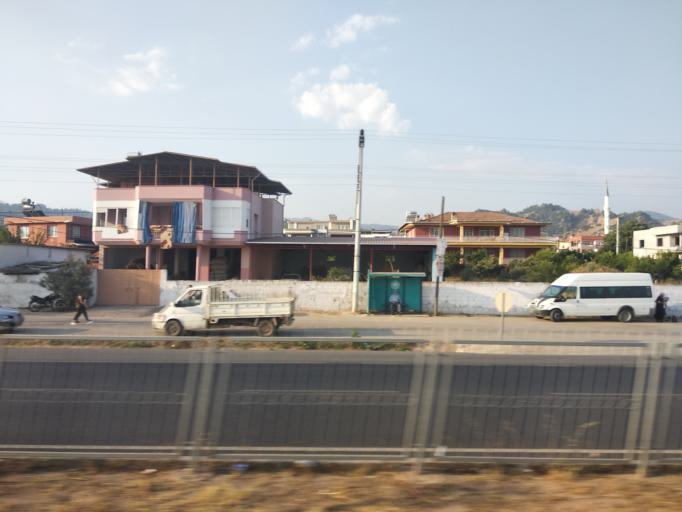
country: TR
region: Manisa
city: Ahmetli
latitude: 38.5058
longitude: 28.0000
